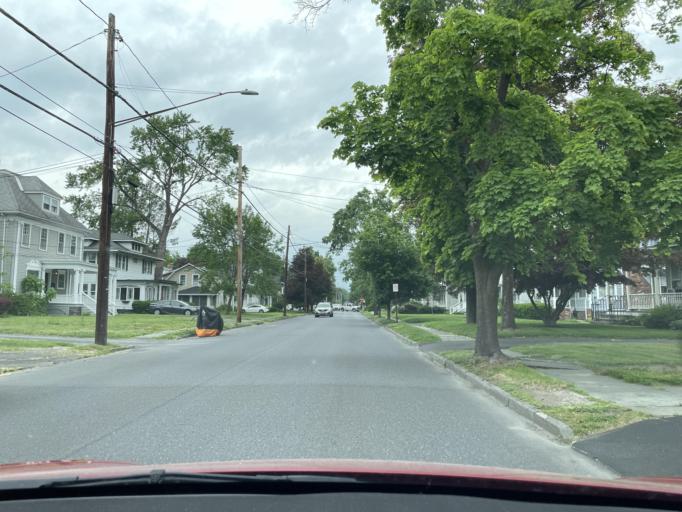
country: US
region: New York
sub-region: Ulster County
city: Kingston
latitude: 41.9292
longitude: -74.0200
